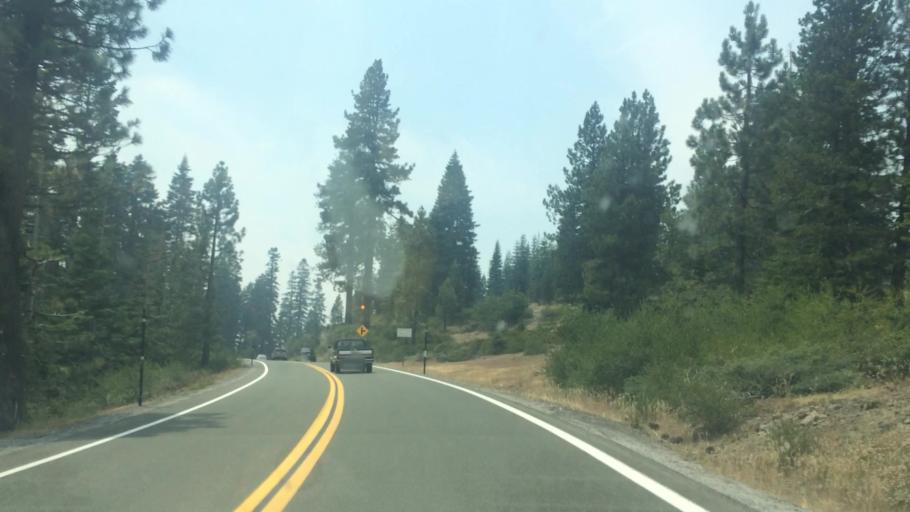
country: US
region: California
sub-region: Calaveras County
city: Arnold
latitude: 38.5838
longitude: -120.2511
